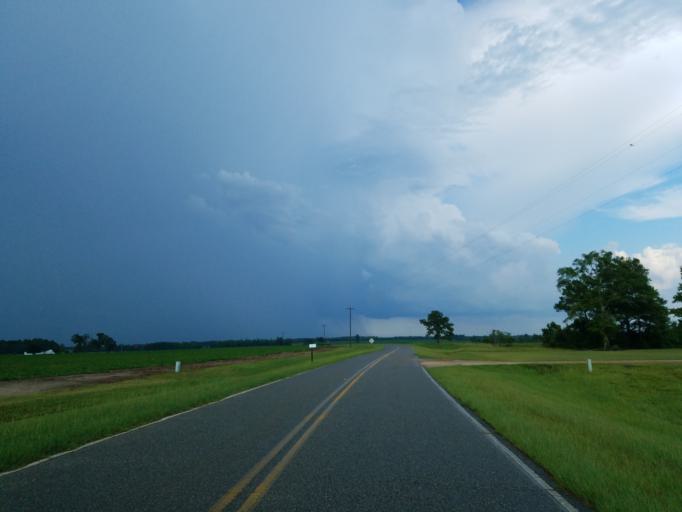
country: US
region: Georgia
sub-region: Cook County
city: Adel
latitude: 31.0676
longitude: -83.4471
